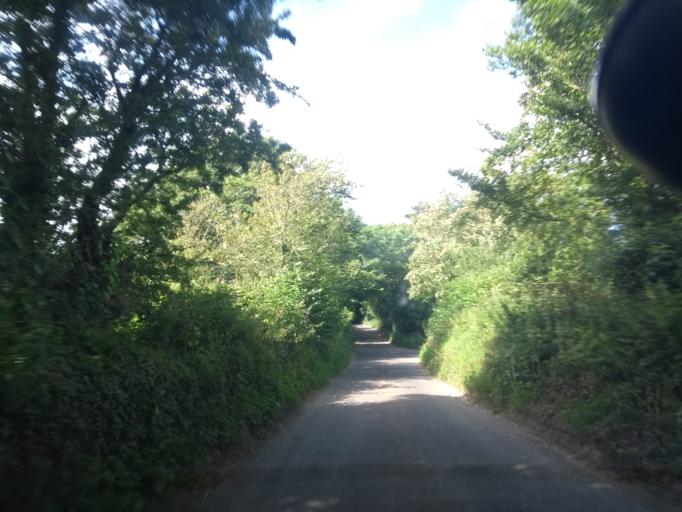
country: GB
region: England
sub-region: Devon
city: Modbury
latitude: 50.3047
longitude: -3.8858
